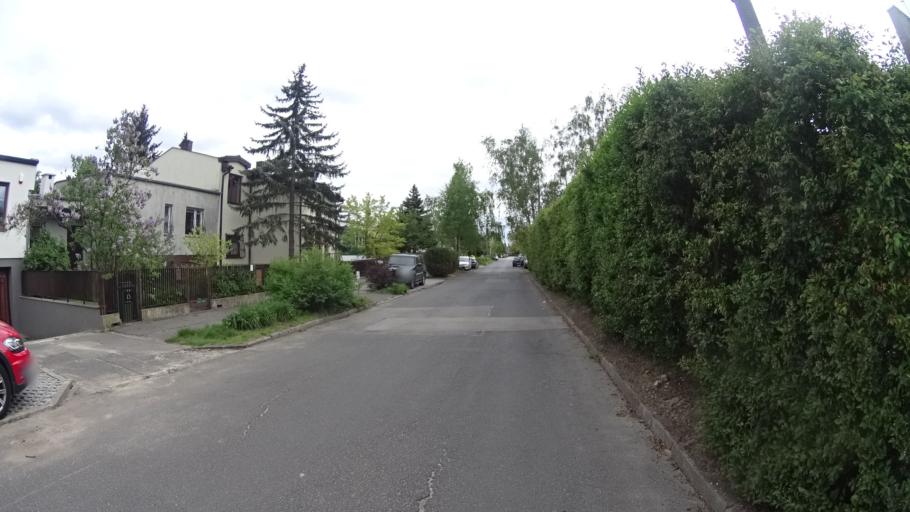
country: PL
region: Masovian Voivodeship
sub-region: Powiat warszawski zachodni
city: Babice
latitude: 52.2521
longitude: 20.8771
